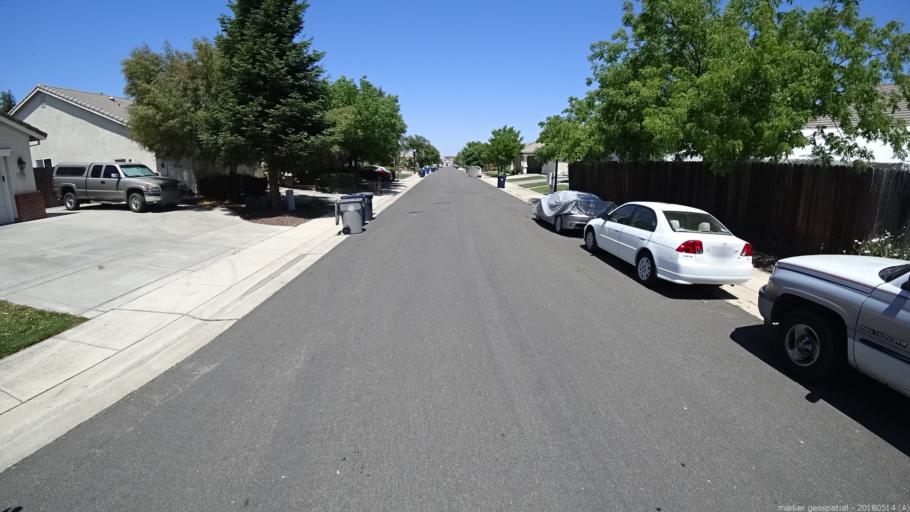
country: US
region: California
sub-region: Yolo County
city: West Sacramento
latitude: 38.6281
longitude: -121.5448
